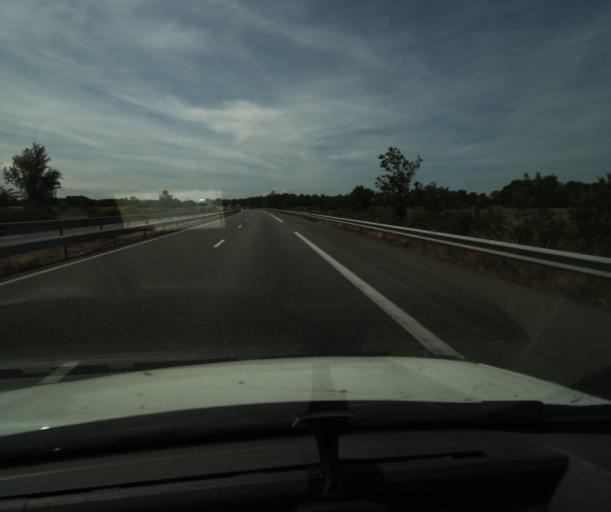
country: FR
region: Languedoc-Roussillon
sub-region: Departement de l'Aude
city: Montreal
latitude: 43.2279
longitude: 2.1473
